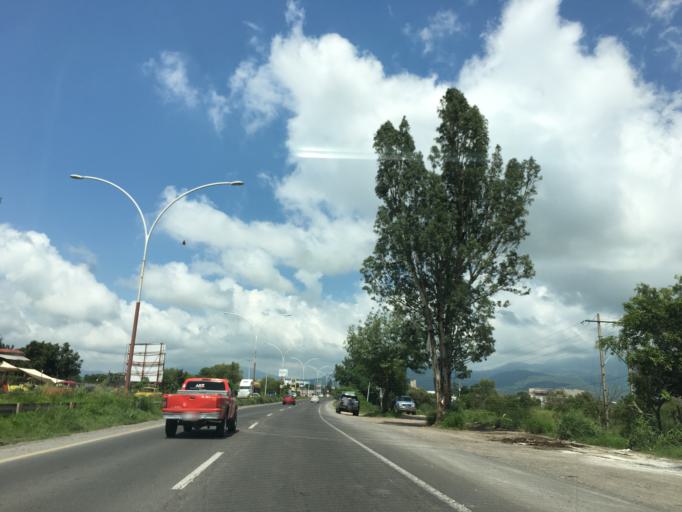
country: MX
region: Nayarit
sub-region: Tepic
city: La Corregidora
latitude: 21.4671
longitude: -104.8535
